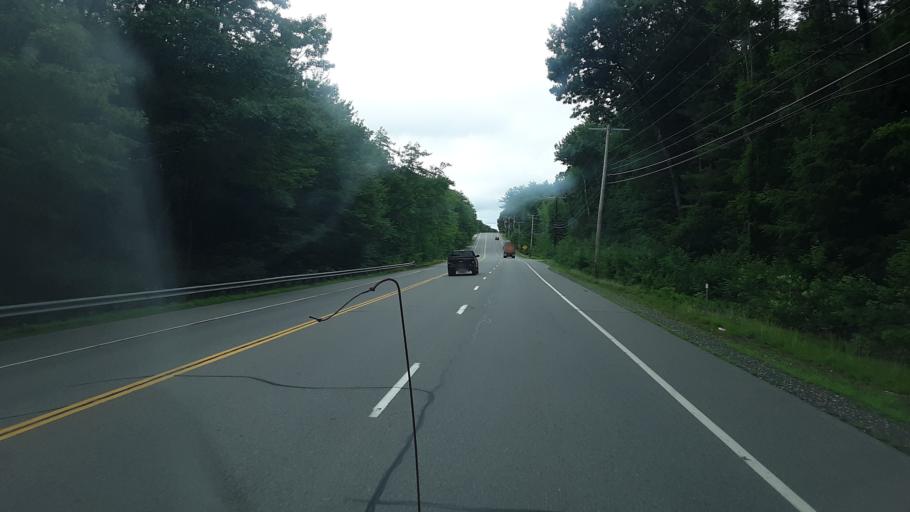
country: US
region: New Hampshire
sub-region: Rockingham County
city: Nottingham
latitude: 43.1653
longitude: -71.0805
